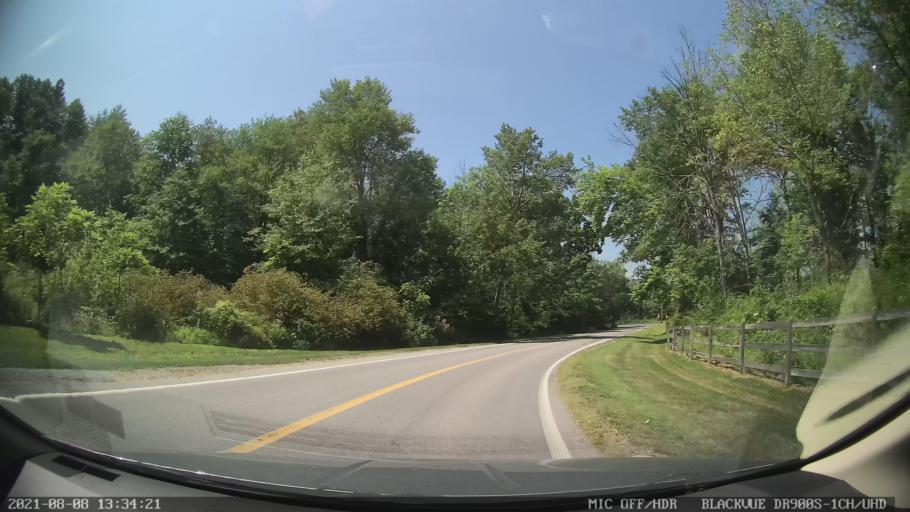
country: US
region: Pennsylvania
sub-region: Berks County
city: Fleetwood
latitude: 40.4478
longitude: -75.7645
